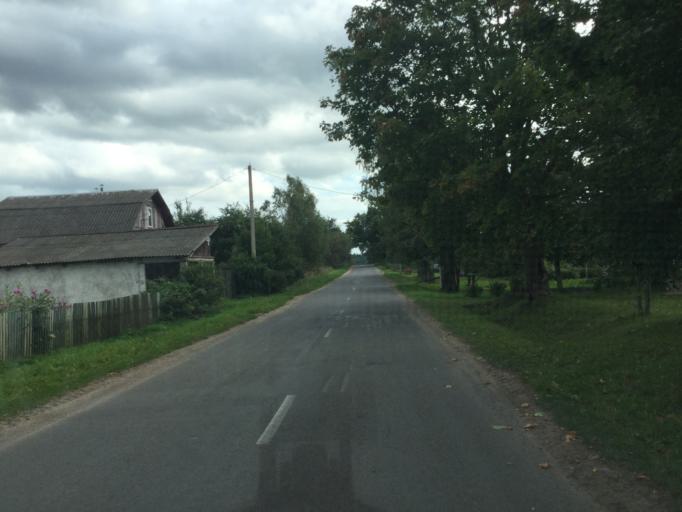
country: BY
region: Vitebsk
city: Vitebsk
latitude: 55.1450
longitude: 30.2842
